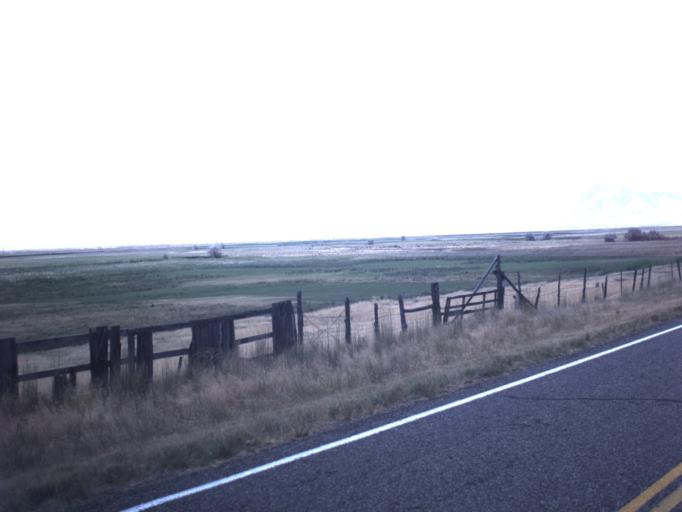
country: US
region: Utah
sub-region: Box Elder County
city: Tremonton
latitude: 41.6243
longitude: -112.3458
